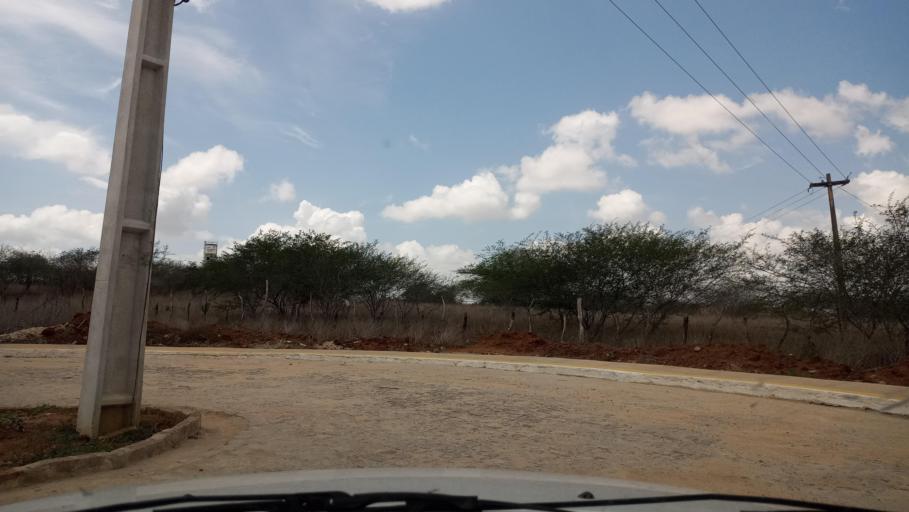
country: BR
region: Rio Grande do Norte
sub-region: Tangara
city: Tangara
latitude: -6.1137
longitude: -35.7175
